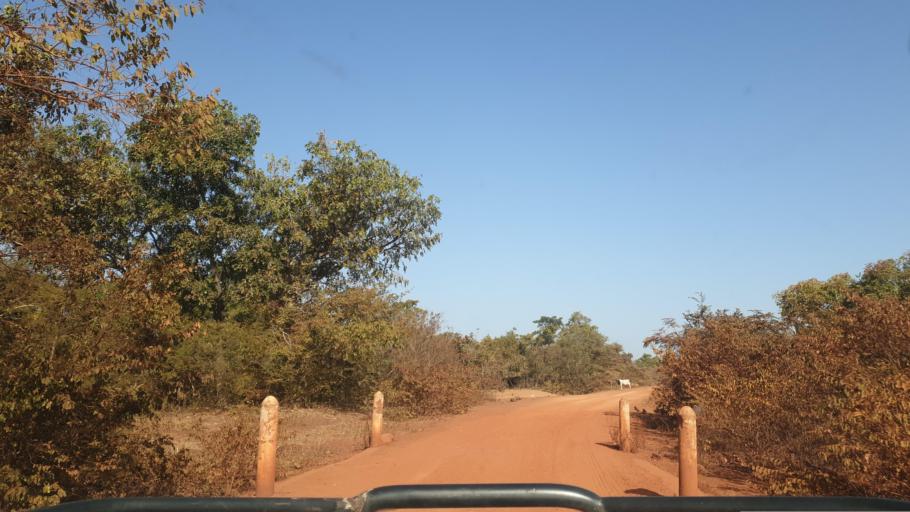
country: ML
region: Sikasso
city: Bougouni
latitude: 11.7784
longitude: -6.9076
